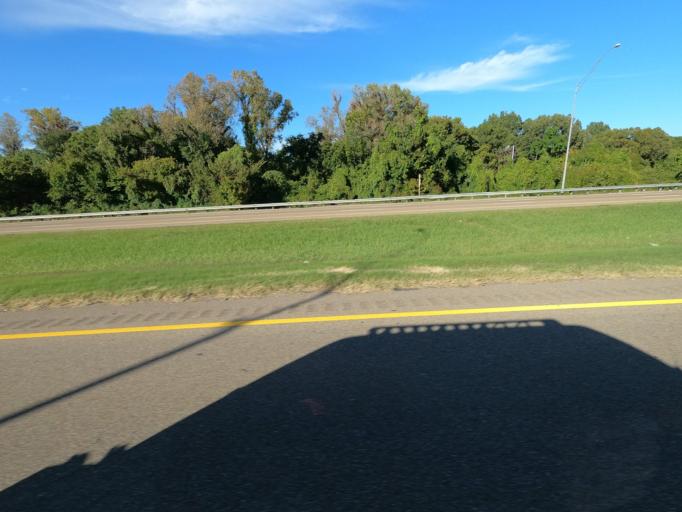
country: US
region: Tennessee
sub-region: Shelby County
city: New South Memphis
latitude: 35.0748
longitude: -90.0378
